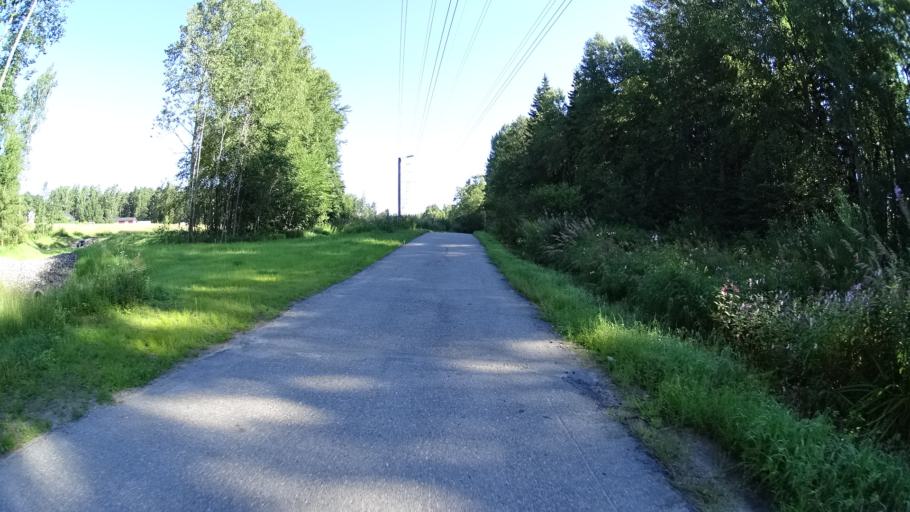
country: FI
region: Uusimaa
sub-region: Helsinki
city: Teekkarikylae
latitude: 60.2549
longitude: 24.8777
